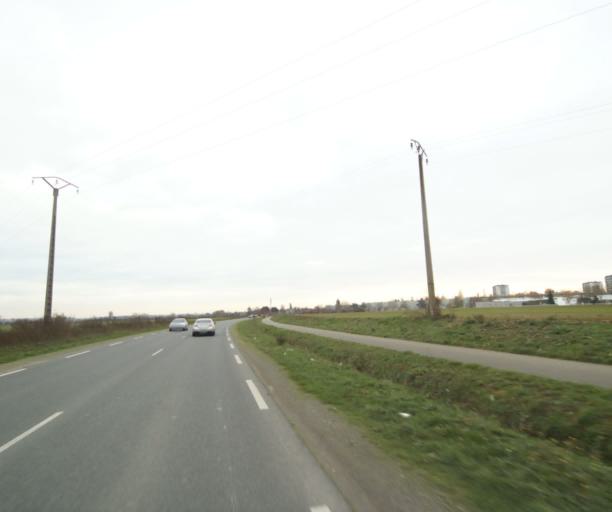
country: FR
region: Ile-de-France
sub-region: Departement du Val-d'Oise
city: Arnouville
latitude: 49.0077
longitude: 2.4254
